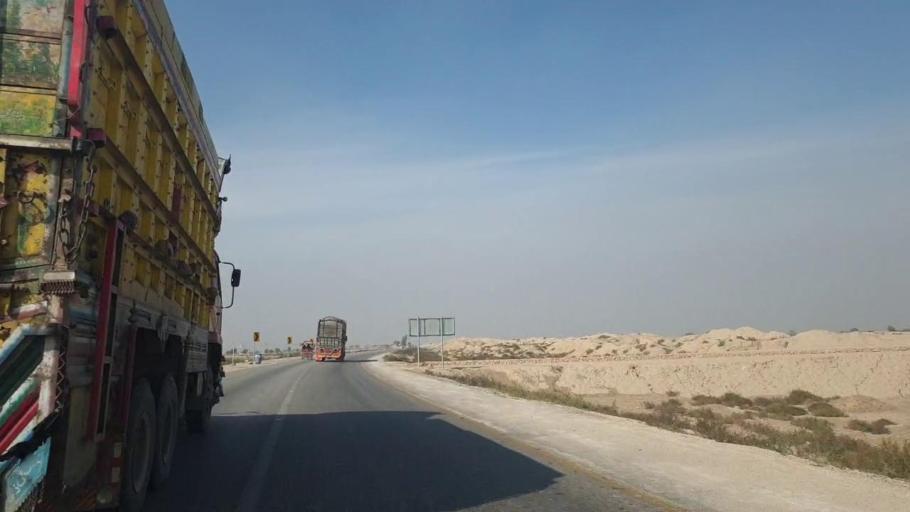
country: PK
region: Sindh
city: Sann
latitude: 25.9548
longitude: 68.1945
